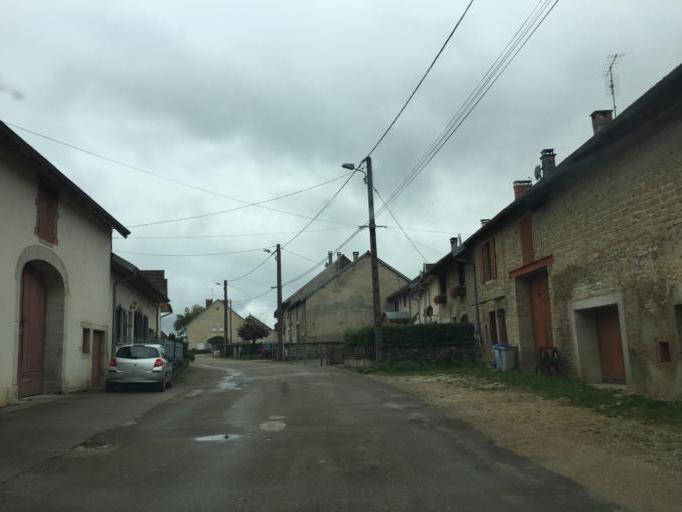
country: FR
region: Franche-Comte
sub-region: Departement du Jura
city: Orgelet
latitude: 46.5604
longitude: 5.6088
